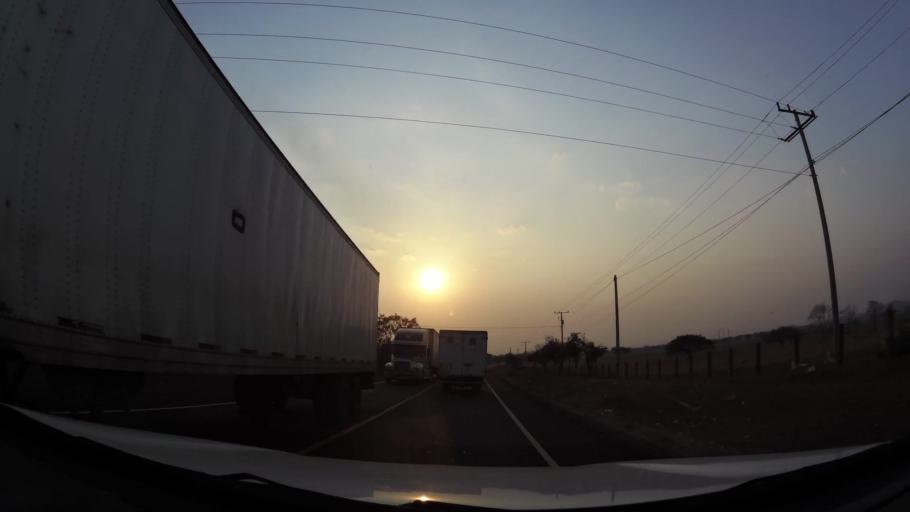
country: NI
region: Leon
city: La Paz Centro
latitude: 12.3307
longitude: -86.6445
